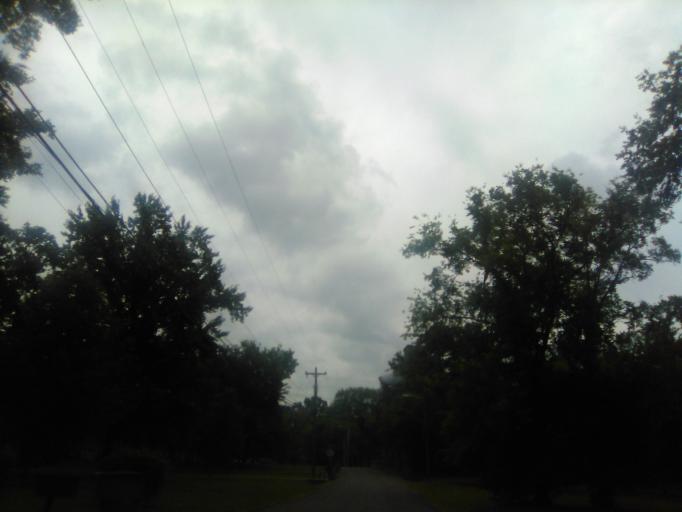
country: US
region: Tennessee
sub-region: Davidson County
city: Belle Meade
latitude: 36.1042
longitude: -86.8786
